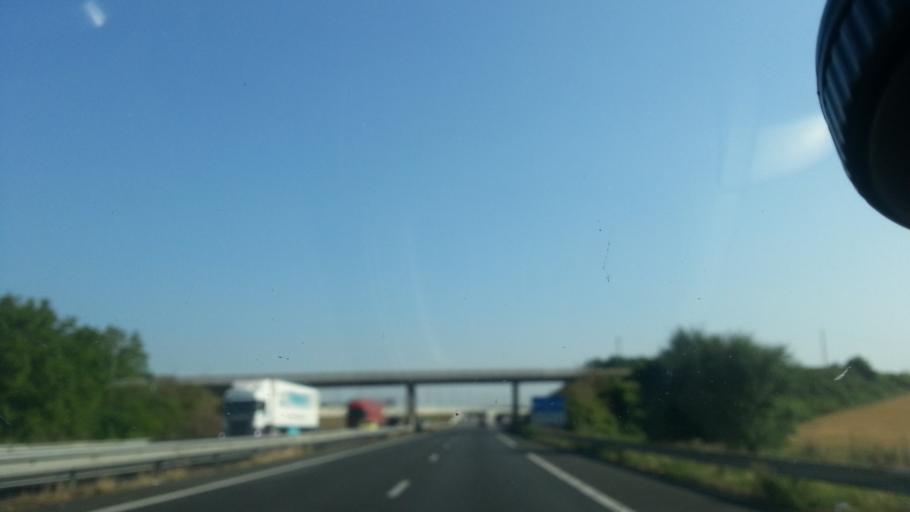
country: FR
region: Centre
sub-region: Departement d'Indre-et-Loire
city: La Celle-Saint-Avant
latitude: 46.9987
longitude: 0.5519
